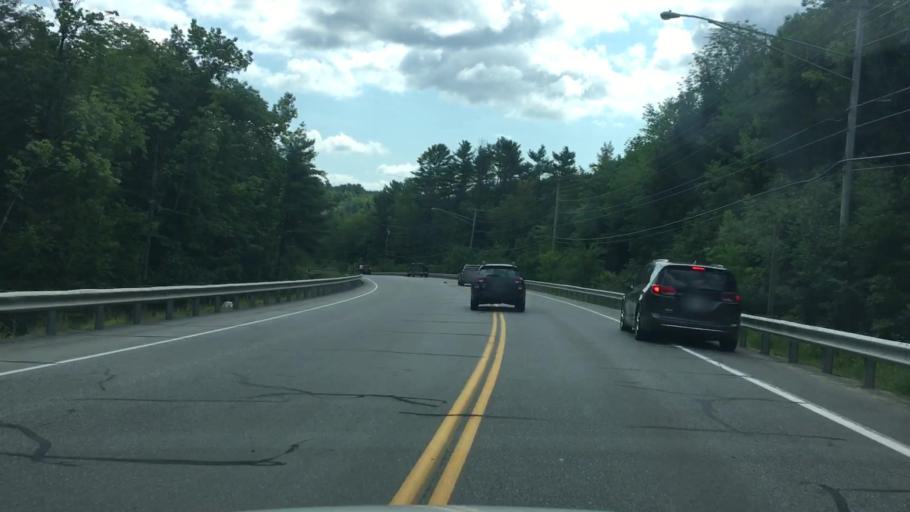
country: US
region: Maine
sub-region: Kennebec County
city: Augusta
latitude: 44.3339
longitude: -69.7930
